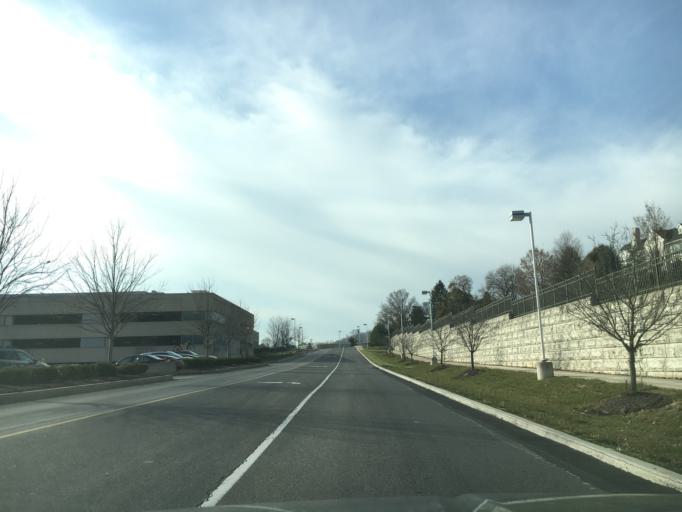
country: US
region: Pennsylvania
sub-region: Montour County
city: Danville
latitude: 40.9699
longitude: -76.6023
